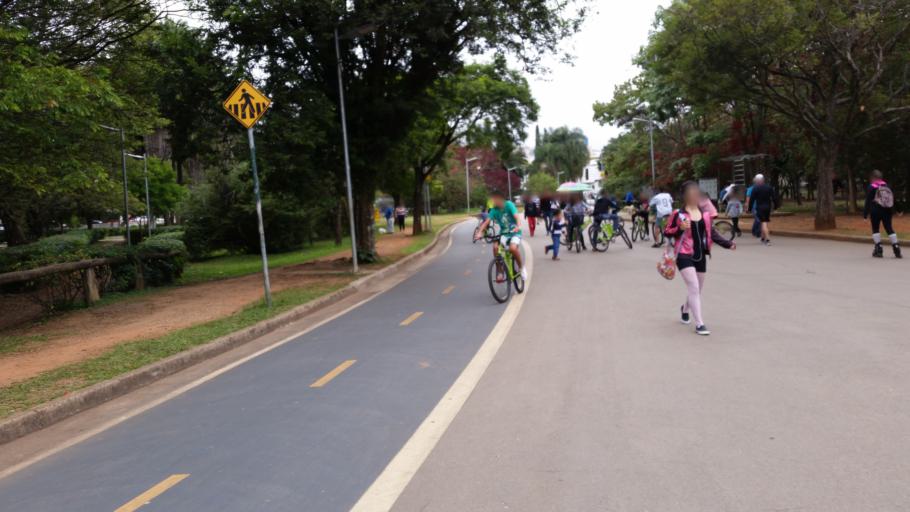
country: BR
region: Sao Paulo
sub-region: Sao Paulo
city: Sao Paulo
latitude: -23.5925
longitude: -46.6600
